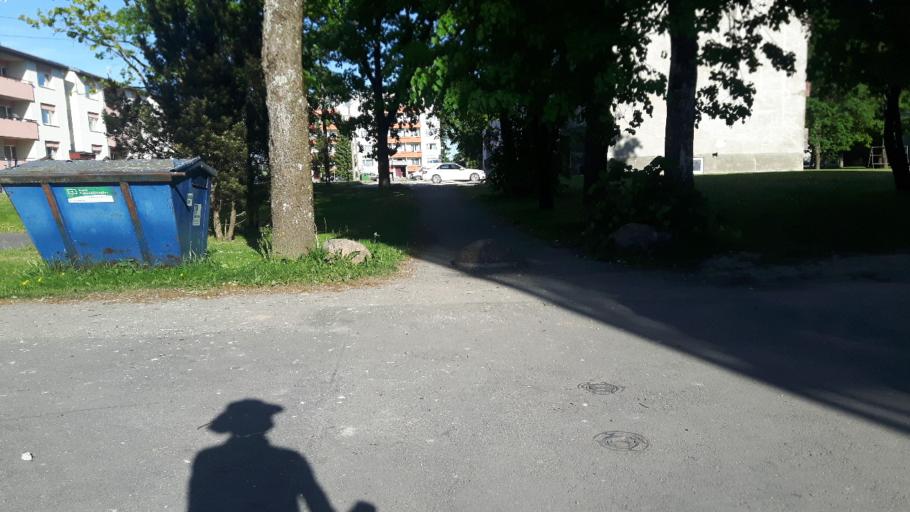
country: EE
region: Raplamaa
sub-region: Kehtna vald
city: Kehtna
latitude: 58.9268
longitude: 24.8729
